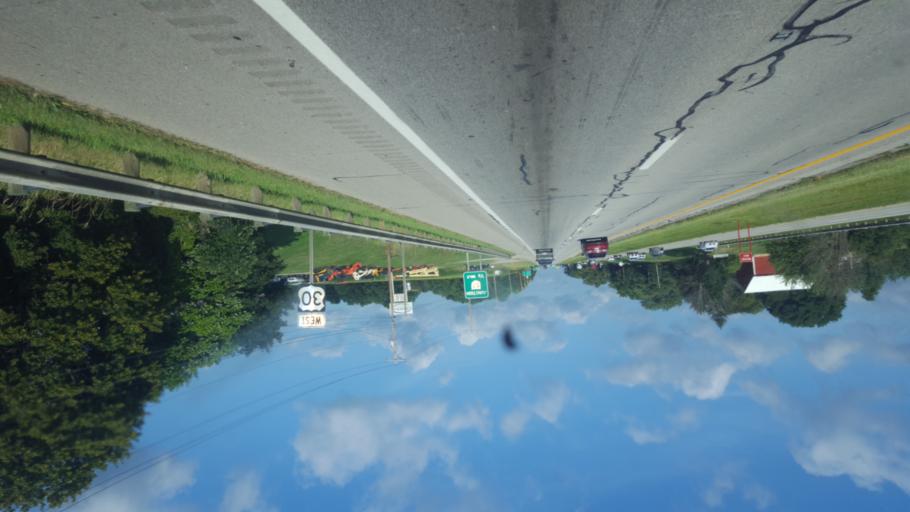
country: US
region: Ohio
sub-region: Wayne County
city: Orrville
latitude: 40.7966
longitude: -81.7556
